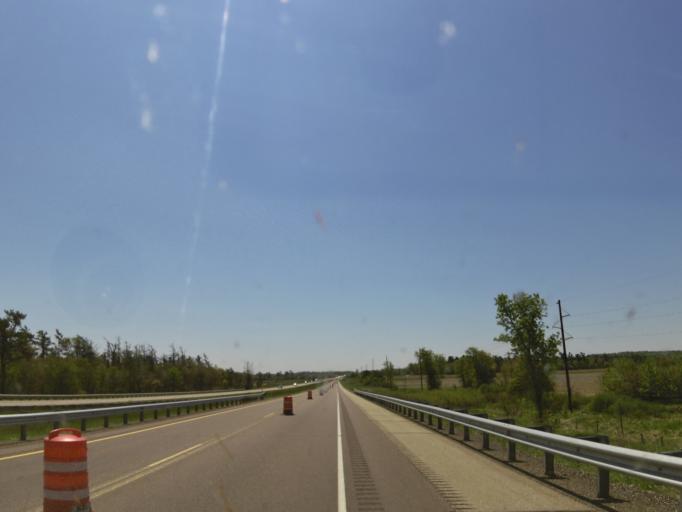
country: US
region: Wisconsin
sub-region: Monroe County
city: Tomah
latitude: 44.0704
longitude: -90.5216
